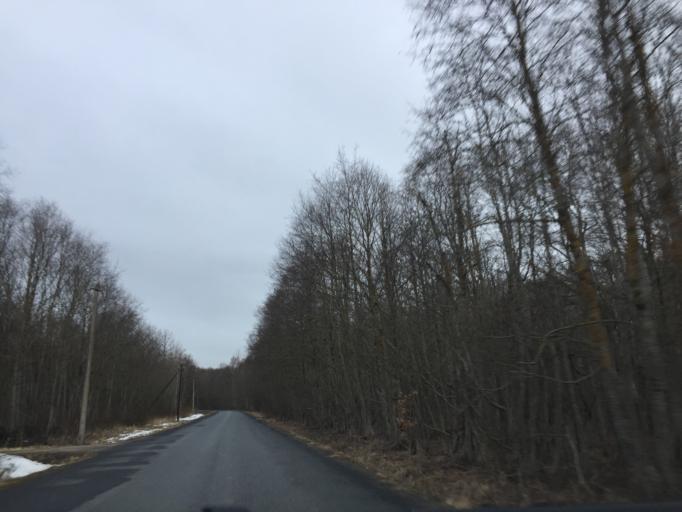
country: EE
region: Laeaene
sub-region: Haapsalu linn
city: Haapsalu
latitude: 58.7988
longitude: 23.4969
